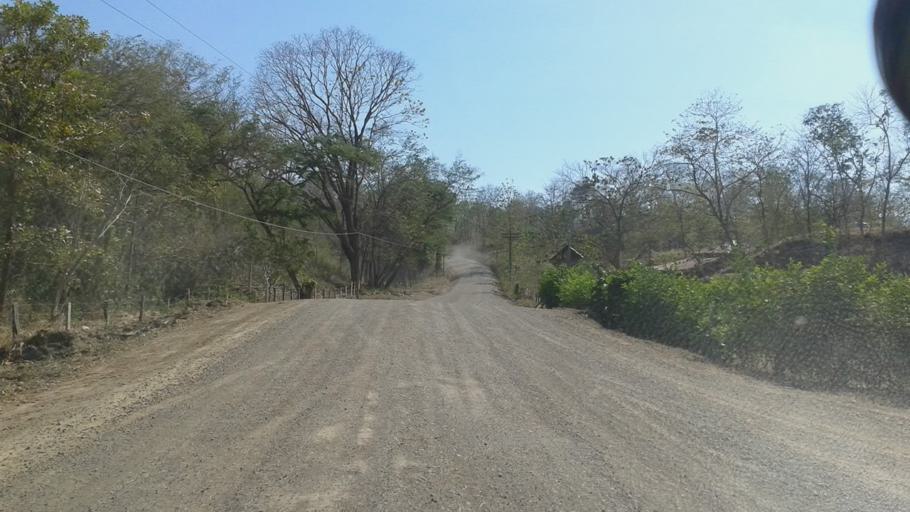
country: CR
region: Guanacaste
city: Santa Cruz
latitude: 10.1841
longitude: -85.7779
